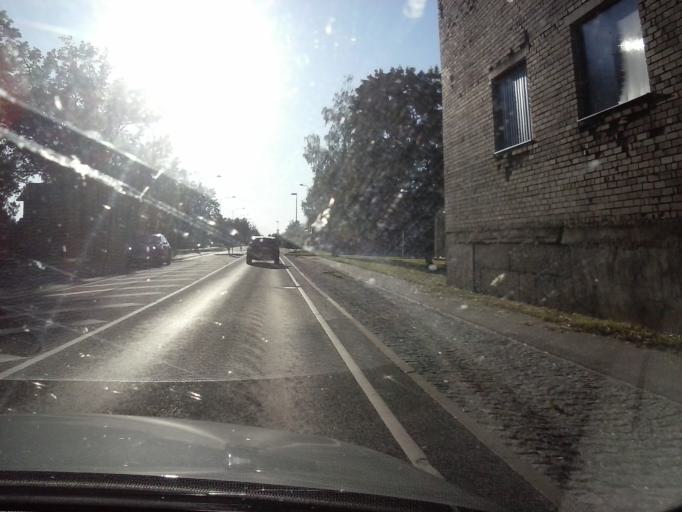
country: EE
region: Raplamaa
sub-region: Rapla vald
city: Rapla
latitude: 58.9925
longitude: 24.8312
